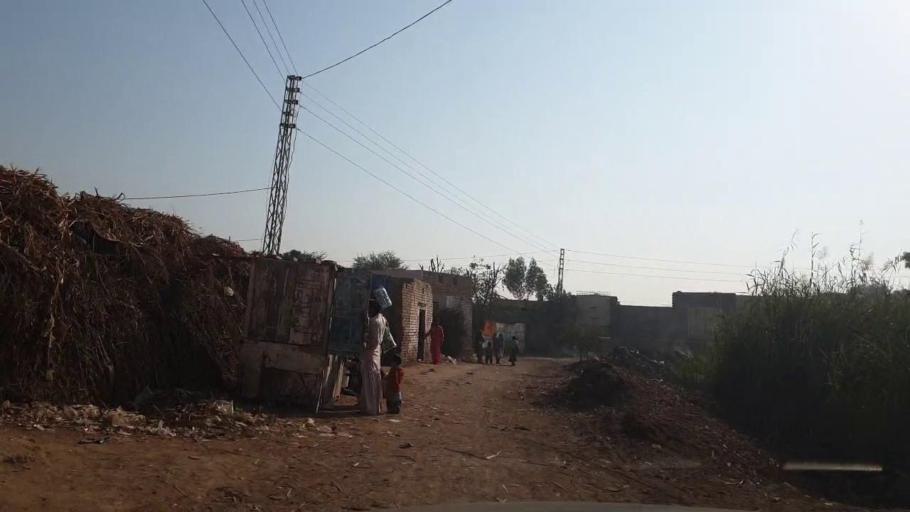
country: PK
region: Sindh
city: Tando Allahyar
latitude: 25.4924
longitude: 68.7322
